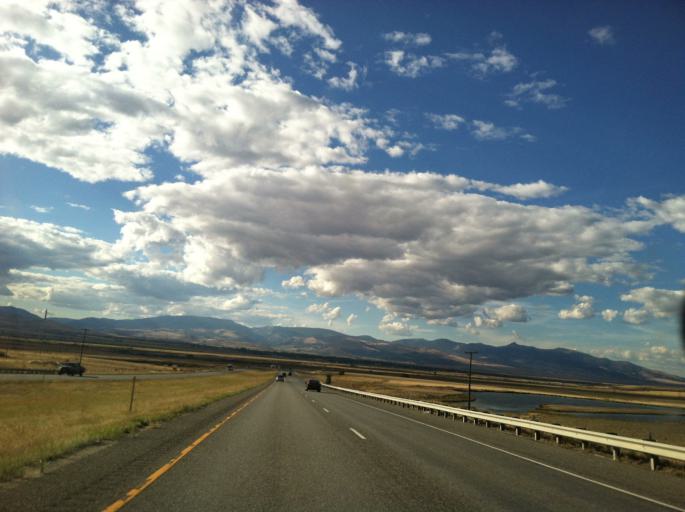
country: US
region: Montana
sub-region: Deer Lodge County
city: Warm Springs
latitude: 46.0664
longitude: -112.7755
